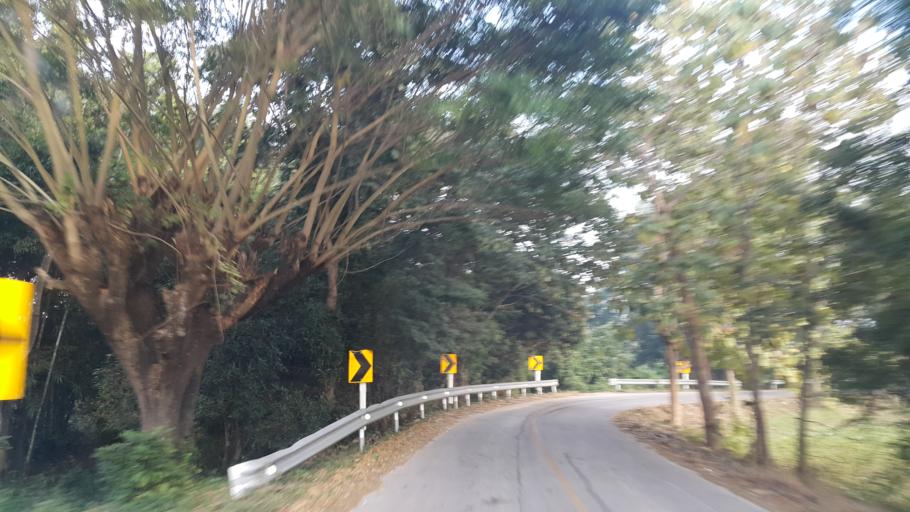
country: TH
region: Lampang
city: Sop Prap
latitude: 17.9150
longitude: 99.3295
